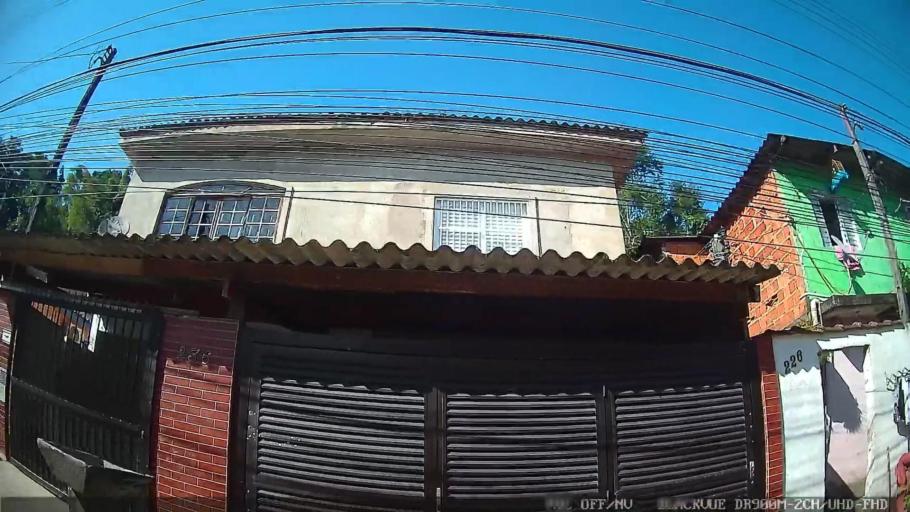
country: BR
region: Sao Paulo
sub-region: Guaruja
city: Guaruja
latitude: -24.0097
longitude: -46.2801
